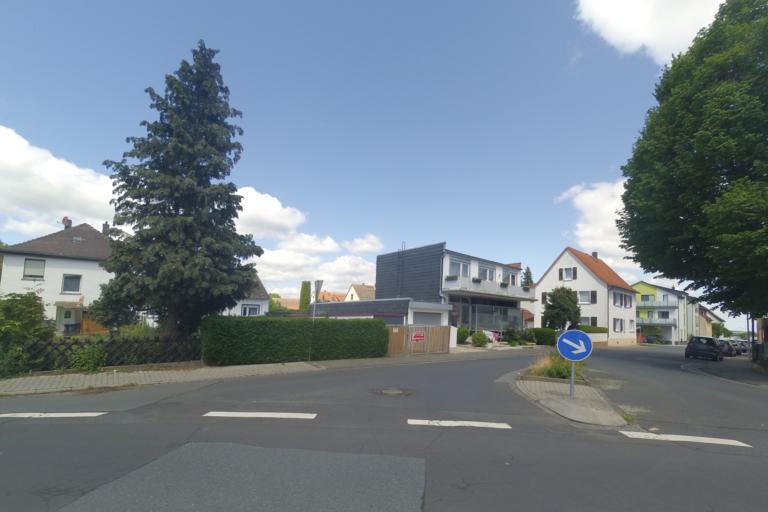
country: DE
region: Hesse
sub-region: Regierungsbezirk Darmstadt
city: Karben
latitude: 50.2421
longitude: 8.7185
